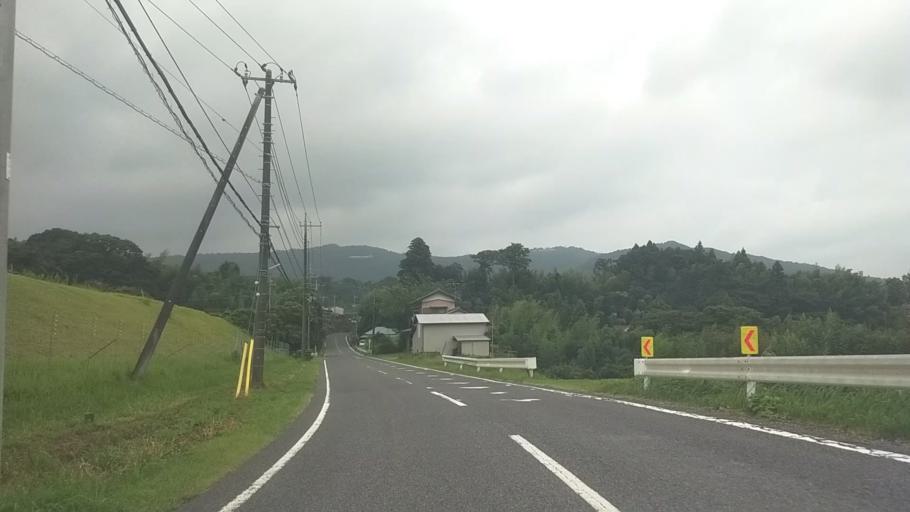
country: JP
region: Chiba
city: Kimitsu
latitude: 35.2440
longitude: 139.9957
